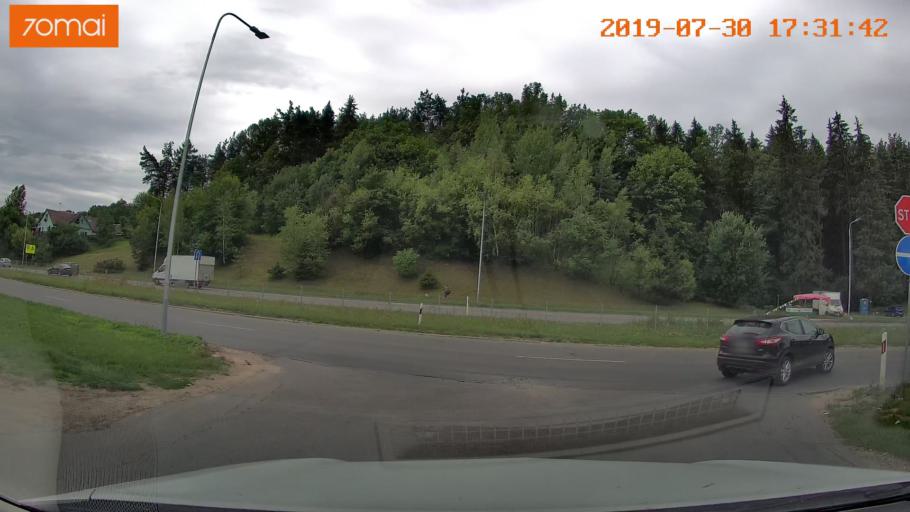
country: LT
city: Skaidiskes
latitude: 54.6903
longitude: 25.3963
